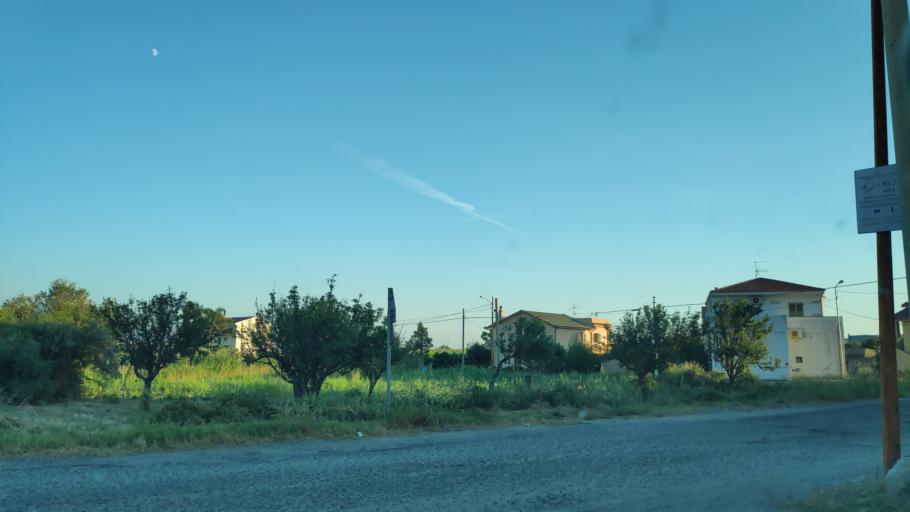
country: IT
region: Calabria
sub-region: Provincia di Reggio Calabria
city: Monasterace Marina
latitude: 38.4344
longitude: 16.5660
